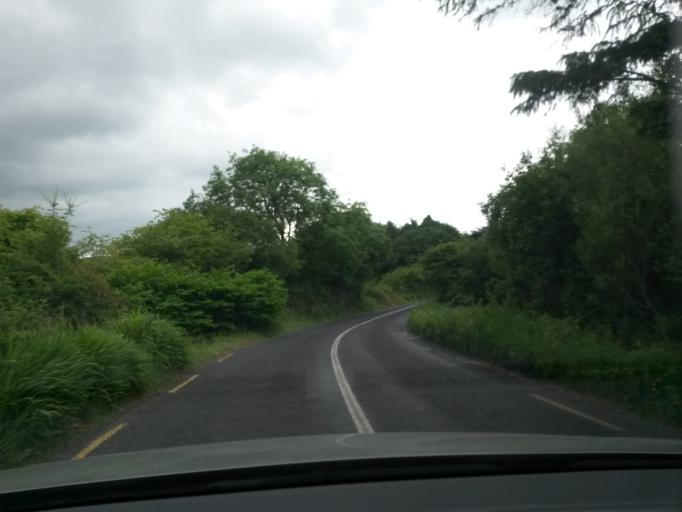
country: IE
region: Connaught
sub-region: County Galway
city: Bearna
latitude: 52.9810
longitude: -9.2418
